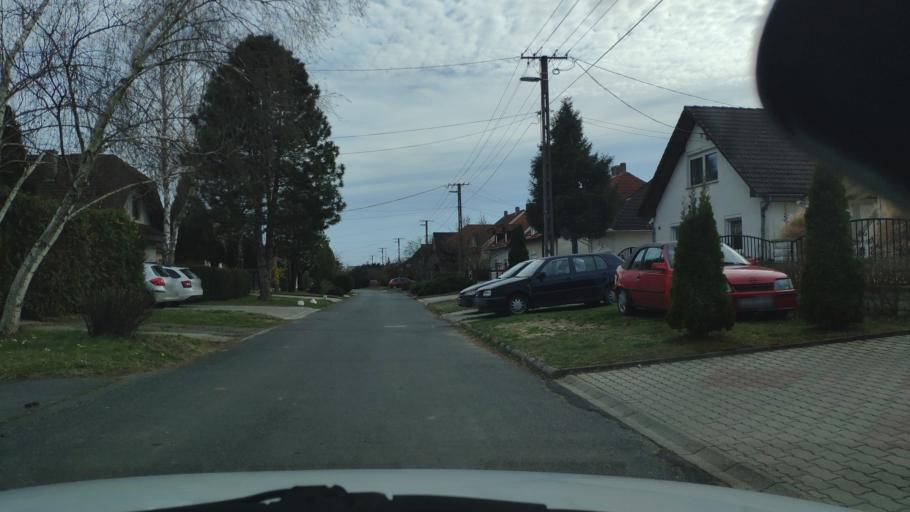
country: HU
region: Zala
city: Nagykanizsa
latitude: 46.4836
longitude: 16.9904
